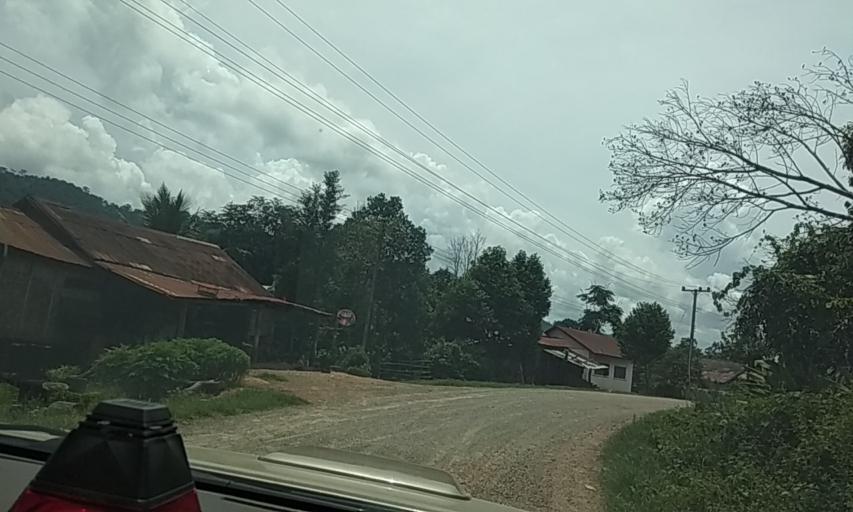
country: LA
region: Bolikhamxai
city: Ban Nahin
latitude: 18.1534
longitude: 104.7223
